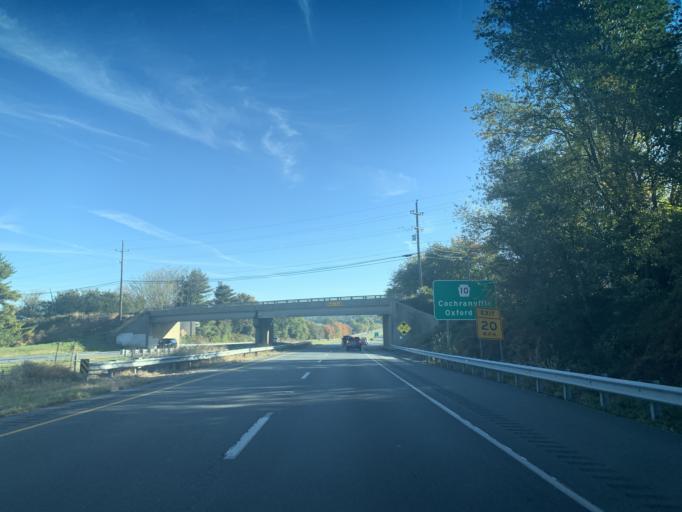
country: US
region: Pennsylvania
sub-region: Chester County
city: Oxford
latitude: 39.8069
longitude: -75.9677
